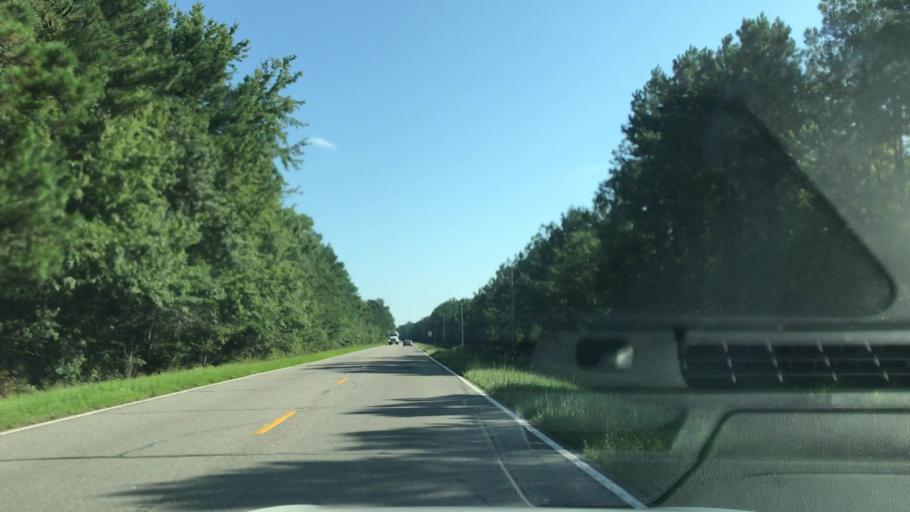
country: US
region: South Carolina
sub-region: Georgetown County
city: Georgetown
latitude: 33.5012
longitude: -79.2582
